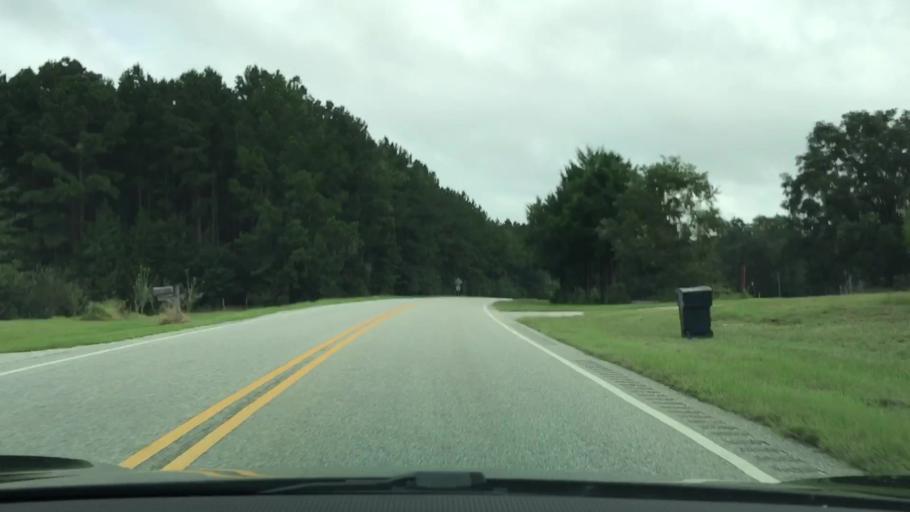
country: US
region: Alabama
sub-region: Geneva County
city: Samson
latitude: 31.0183
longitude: -86.1249
